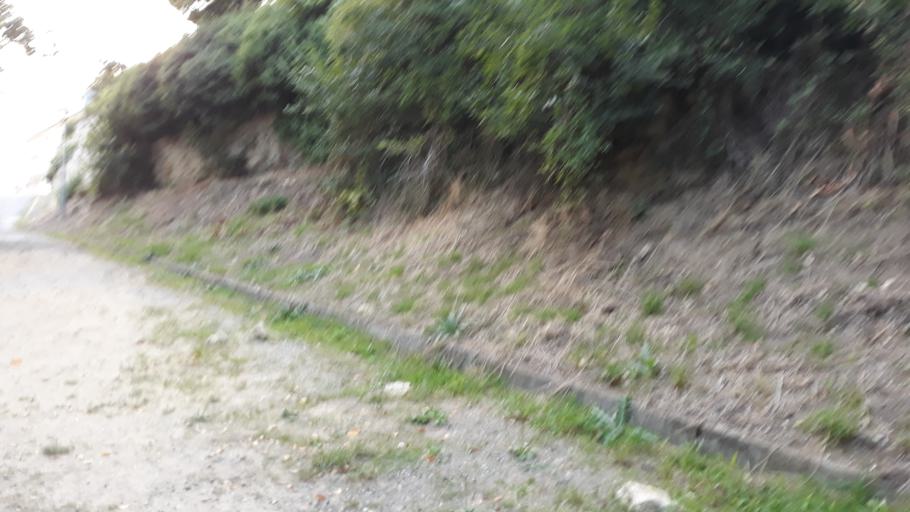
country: FR
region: Picardie
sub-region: Departement de l'Aisne
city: Laon
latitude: 49.5555
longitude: 3.6155
